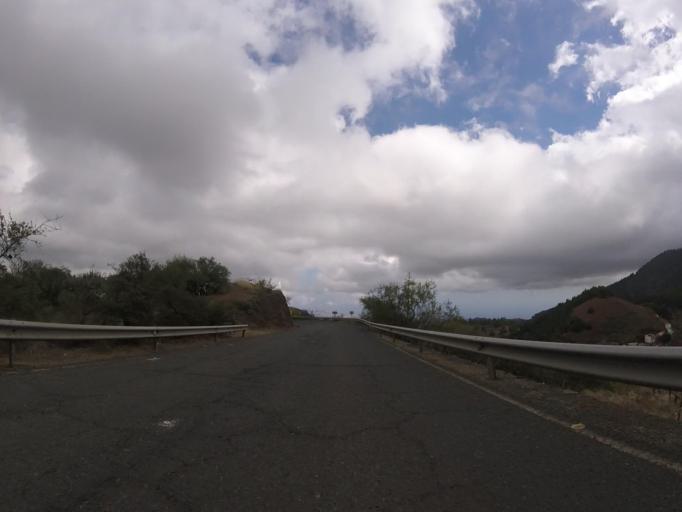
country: ES
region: Canary Islands
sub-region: Provincia de Las Palmas
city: Vega de San Mateo
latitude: 27.9884
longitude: -15.5668
